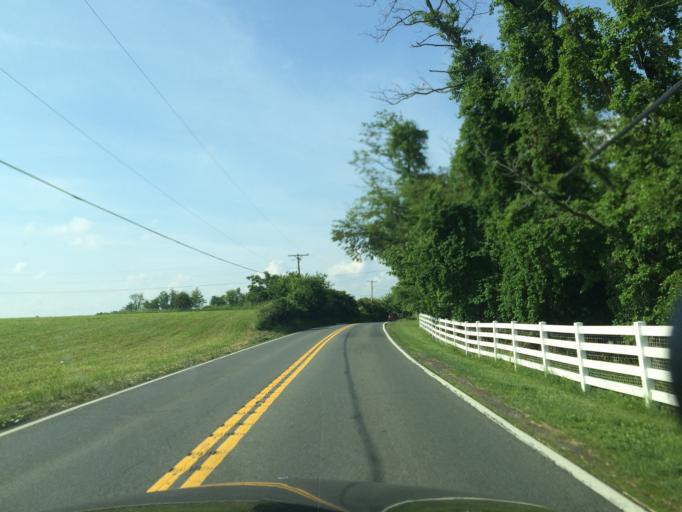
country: US
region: Maryland
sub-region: Montgomery County
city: Olney
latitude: 39.2158
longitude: -77.0613
